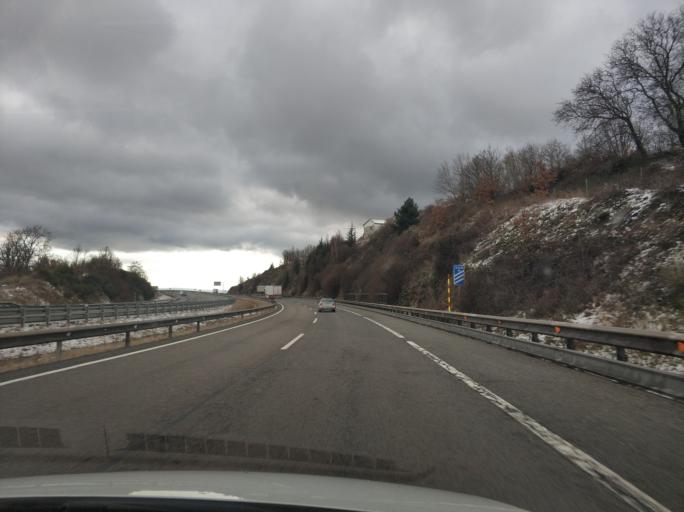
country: ES
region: Madrid
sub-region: Provincia de Madrid
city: Robregordo
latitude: 41.1036
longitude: -3.5928
